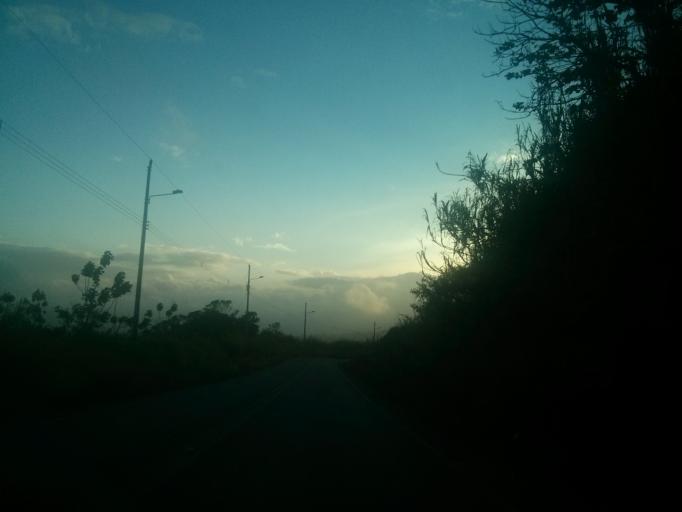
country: CR
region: Cartago
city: Cot
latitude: 9.8841
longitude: -83.8907
